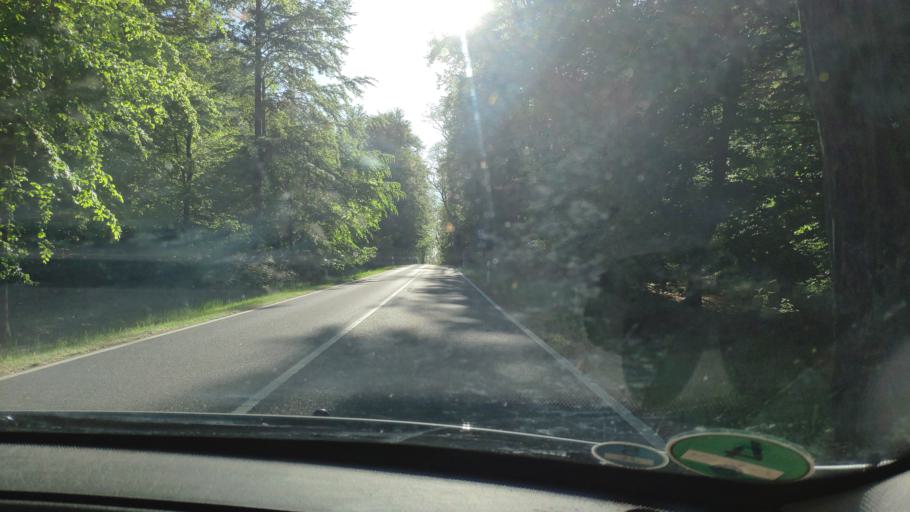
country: DE
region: Mecklenburg-Vorpommern
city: Wesenberg
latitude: 53.3211
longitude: 12.9573
